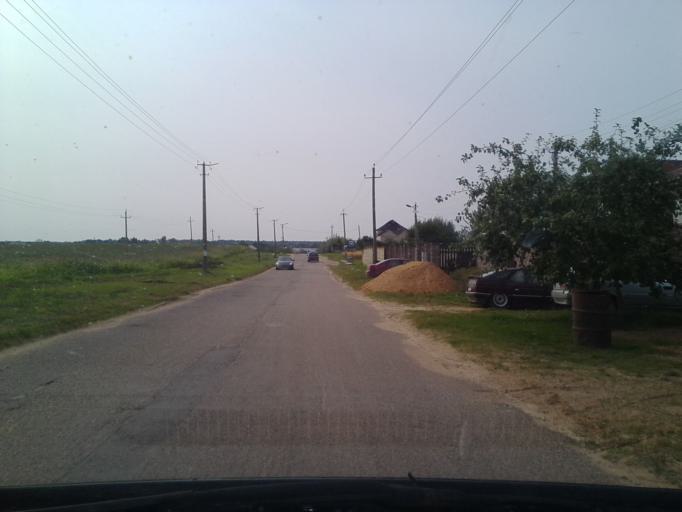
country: BY
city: Michanovichi
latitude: 53.7624
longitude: 27.6892
